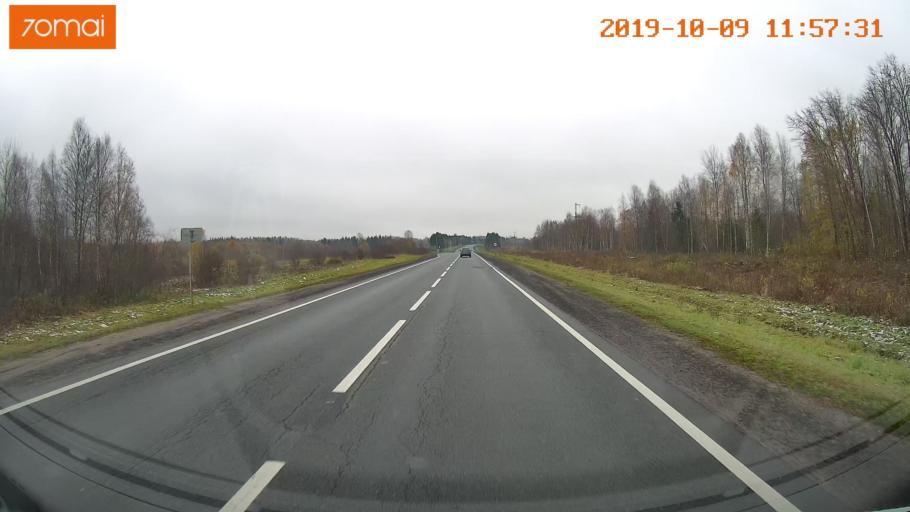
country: RU
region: Vologda
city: Gryazovets
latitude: 58.7312
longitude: 40.2930
